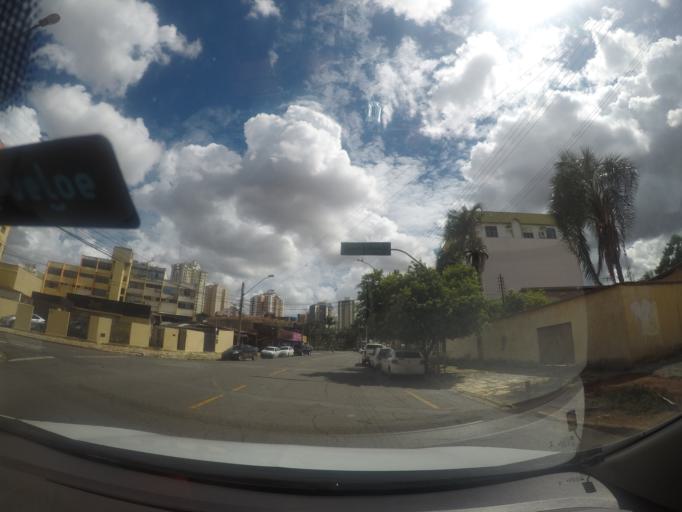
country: BR
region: Goias
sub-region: Goiania
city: Goiania
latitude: -16.6856
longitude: -49.2778
